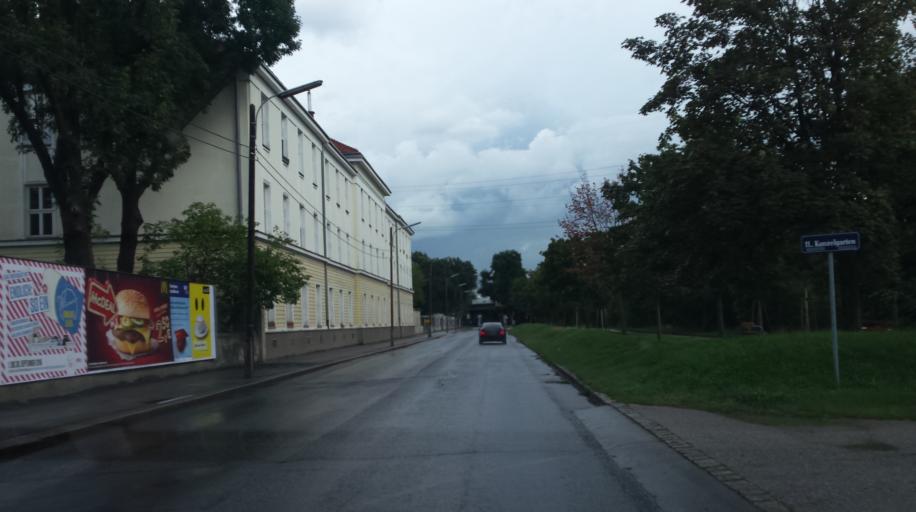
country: AT
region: Lower Austria
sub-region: Politischer Bezirk Wien-Umgebung
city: Schwechat
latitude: 48.1664
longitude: 16.4706
